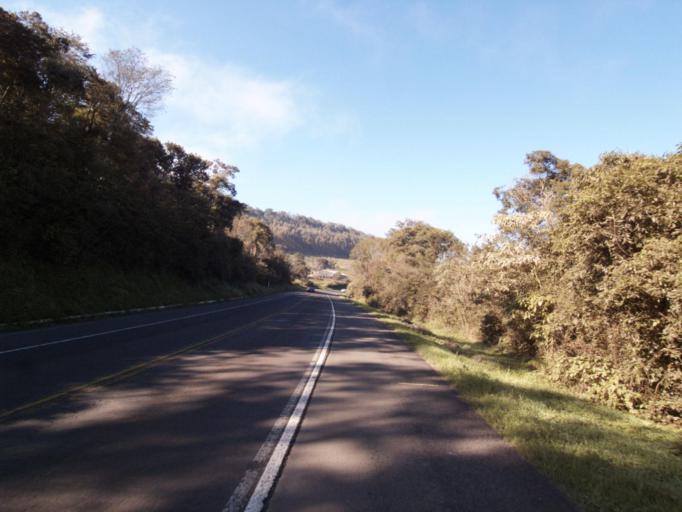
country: BR
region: Rio Grande do Sul
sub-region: Frederico Westphalen
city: Frederico Westphalen
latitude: -26.9890
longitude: -53.2265
